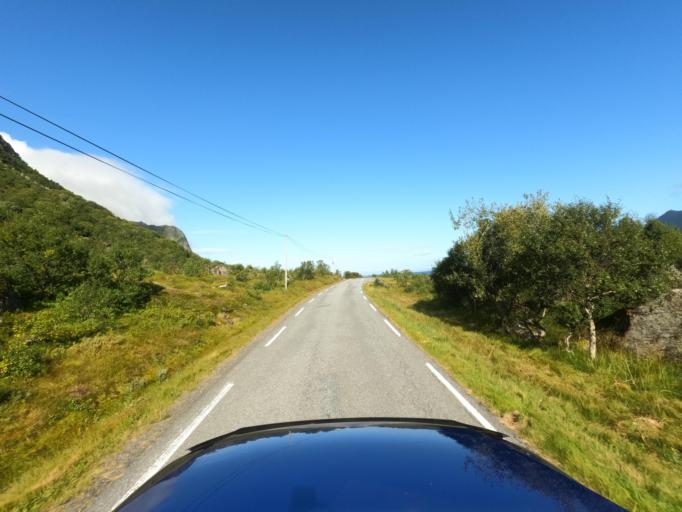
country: NO
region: Nordland
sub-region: Vagan
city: Kabelvag
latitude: 68.2982
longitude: 14.2664
